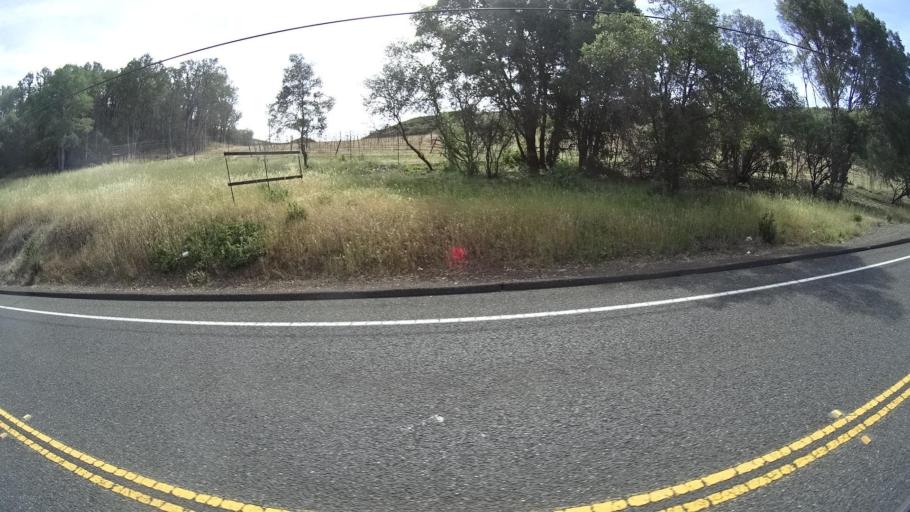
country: US
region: California
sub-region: Lake County
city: Soda Bay
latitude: 38.9398
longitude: -122.7391
